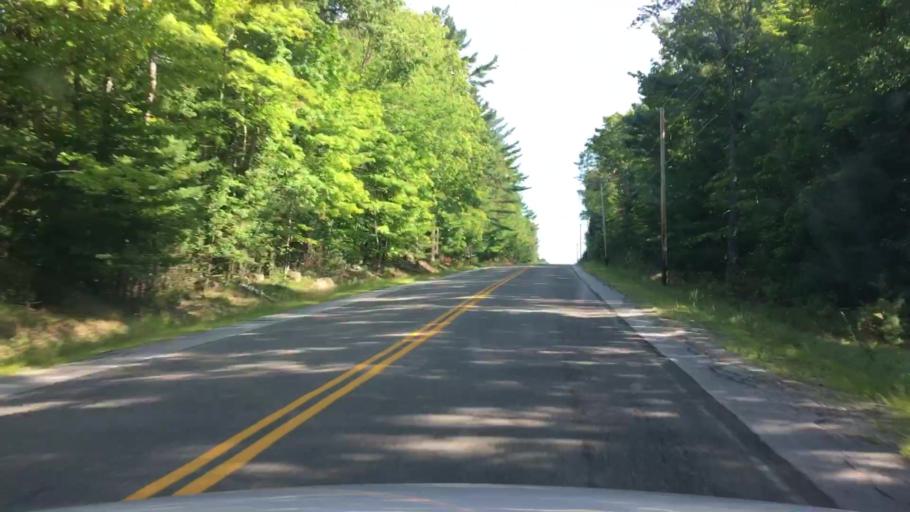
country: US
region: Maine
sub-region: Penobscot County
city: Enfield
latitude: 45.2125
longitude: -68.5253
